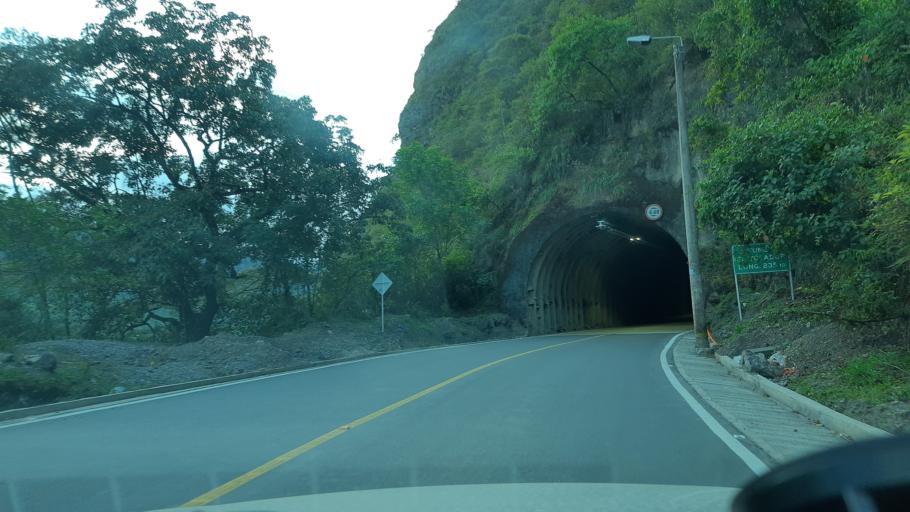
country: CO
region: Boyaca
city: Somondoco
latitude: 4.9860
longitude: -73.3474
